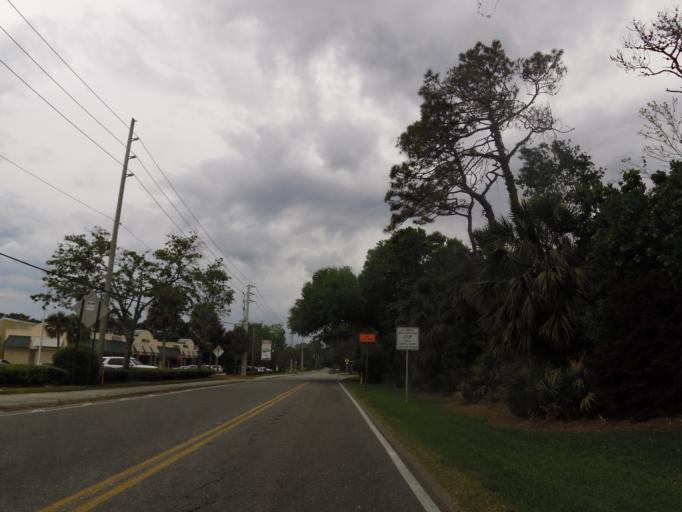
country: US
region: Florida
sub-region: Saint Johns County
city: Ponte Vedra Beach
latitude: 30.2274
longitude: -81.3878
